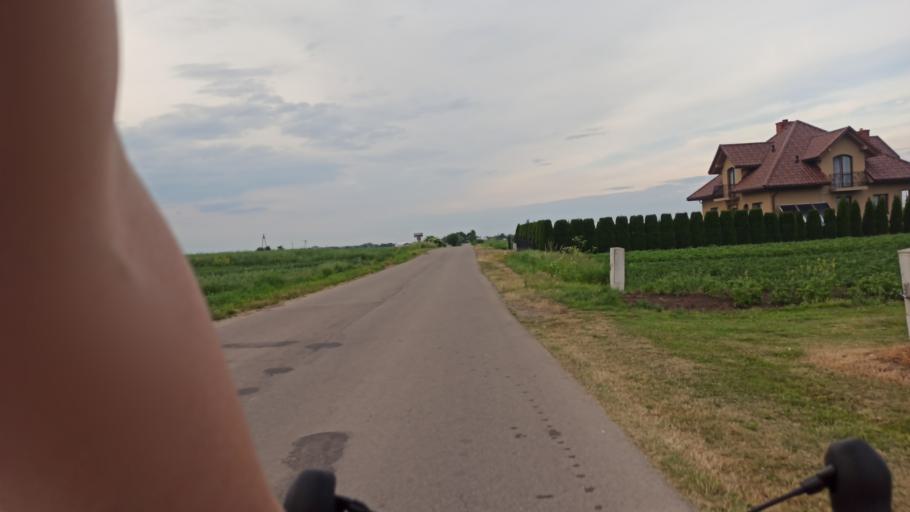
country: PL
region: Subcarpathian Voivodeship
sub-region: Powiat jaroslawski
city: Radymno
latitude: 49.9230
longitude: 22.8005
